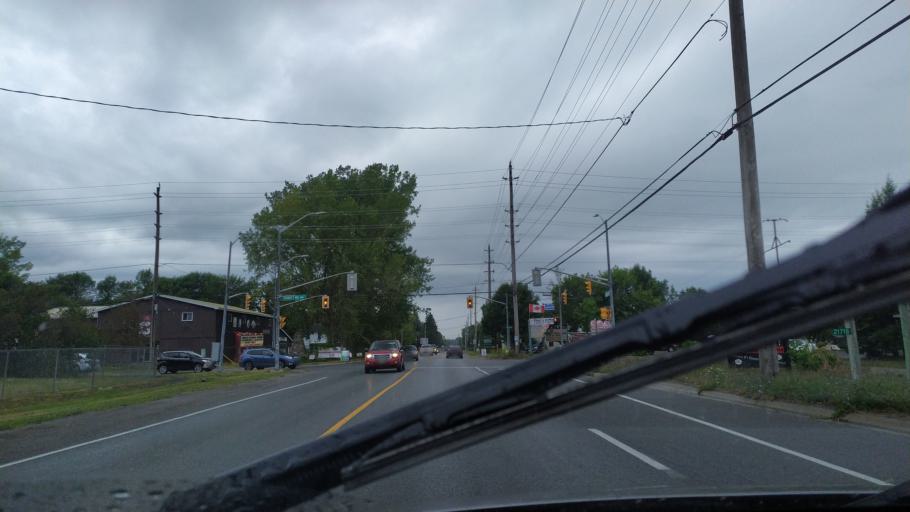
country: CA
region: Ontario
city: Quinte West
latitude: 44.0485
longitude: -77.5811
